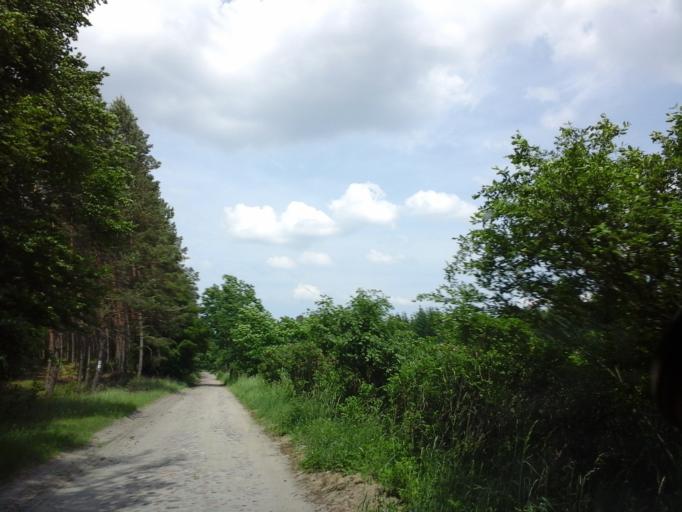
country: PL
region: West Pomeranian Voivodeship
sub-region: Powiat choszczenski
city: Drawno
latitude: 53.1649
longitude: 15.7918
